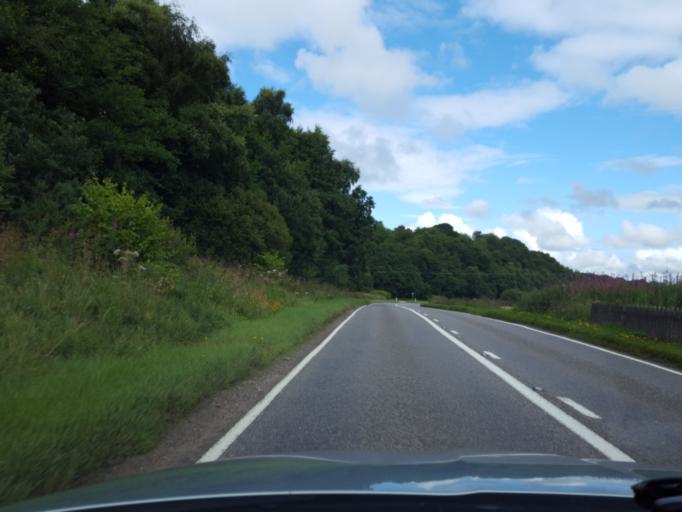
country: GB
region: Scotland
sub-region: Moray
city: Rothes
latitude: 57.5083
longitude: -3.2011
